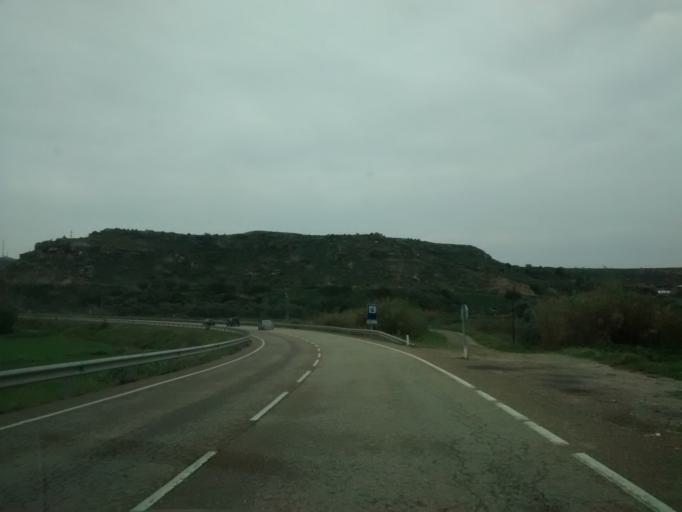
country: ES
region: Aragon
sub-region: Provincia de Zaragoza
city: Caspe
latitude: 41.2541
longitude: -0.0701
